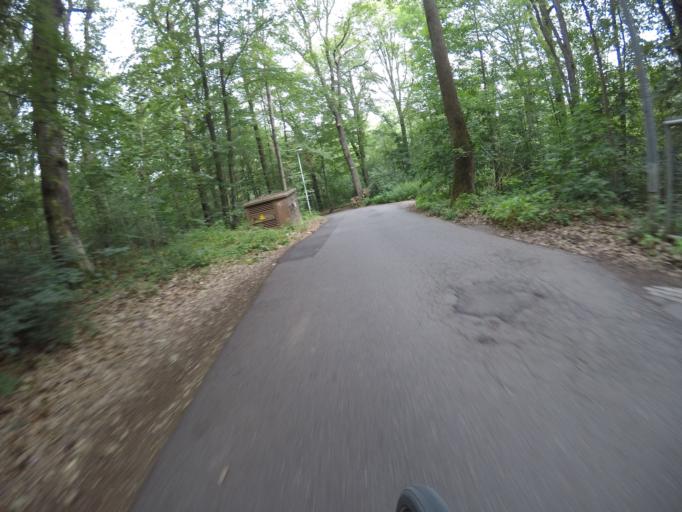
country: DE
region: Baden-Wuerttemberg
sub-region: Regierungsbezirk Stuttgart
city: Stuttgart-Ost
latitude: 48.7737
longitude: 9.2212
